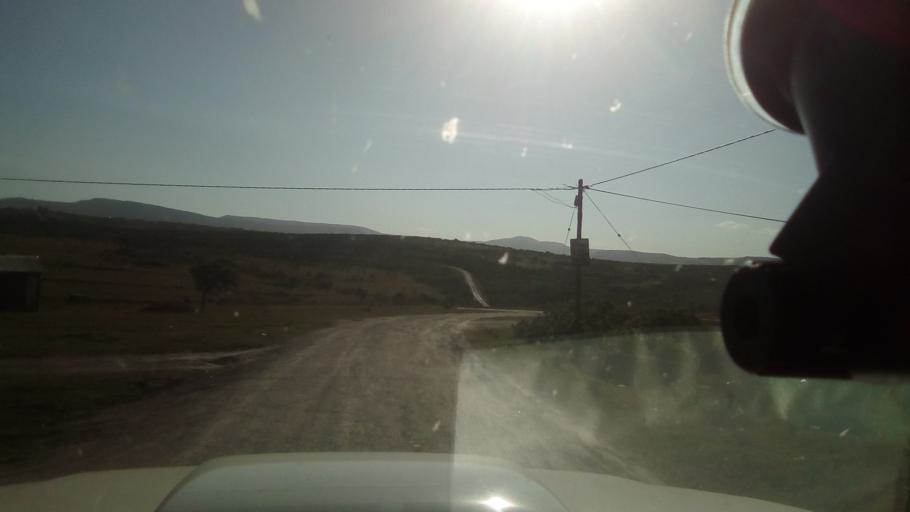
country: ZA
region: Eastern Cape
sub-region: Buffalo City Metropolitan Municipality
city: Bhisho
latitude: -32.7966
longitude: 27.3453
